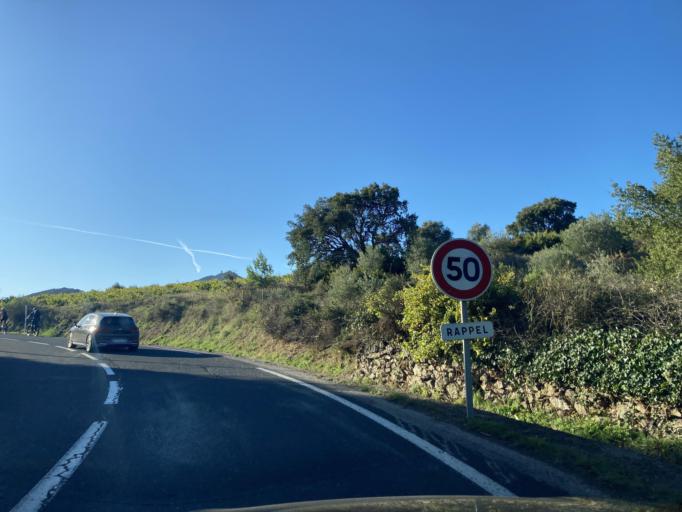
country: FR
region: Languedoc-Roussillon
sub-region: Departement des Pyrenees-Orientales
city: Collioure
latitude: 42.5265
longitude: 3.0741
